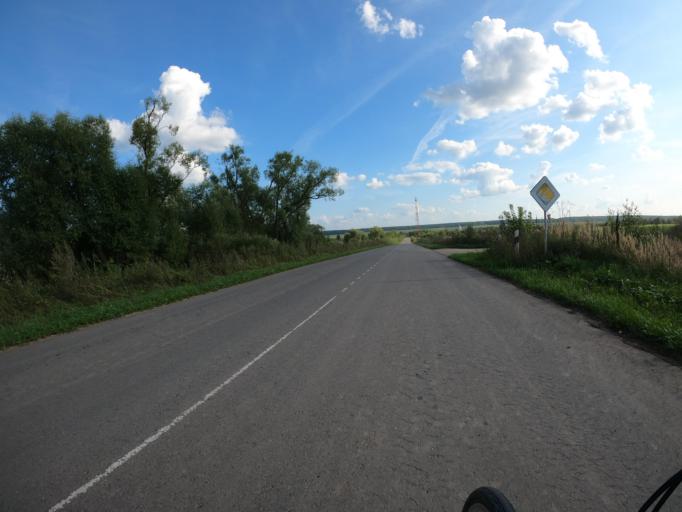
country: RU
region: Moskovskaya
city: Troitskoye
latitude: 55.2017
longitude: 38.4887
